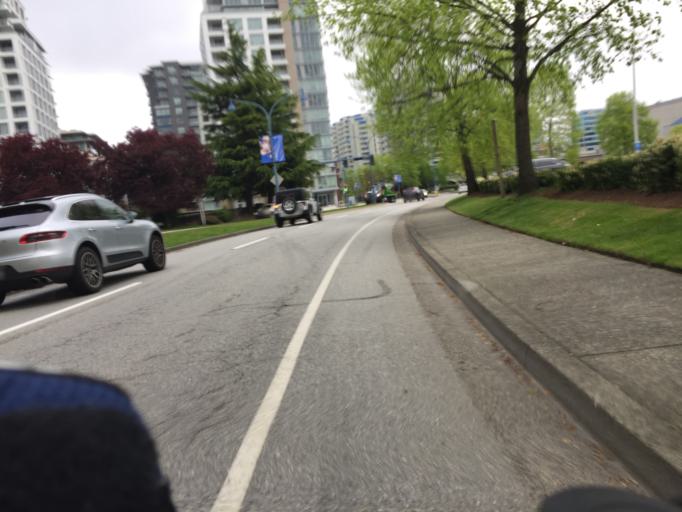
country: CA
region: British Columbia
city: Richmond
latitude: 49.1662
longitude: -123.1410
